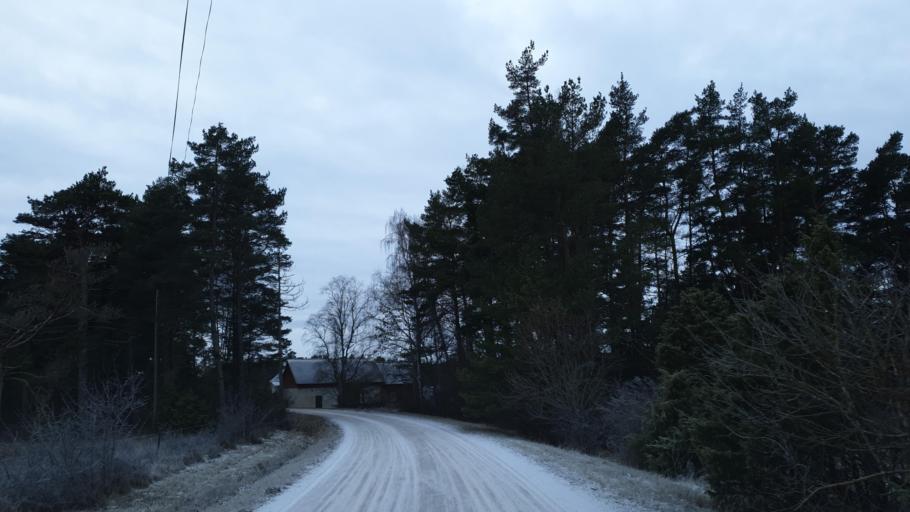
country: SE
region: Gotland
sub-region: Gotland
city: Slite
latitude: 57.4304
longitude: 18.8124
